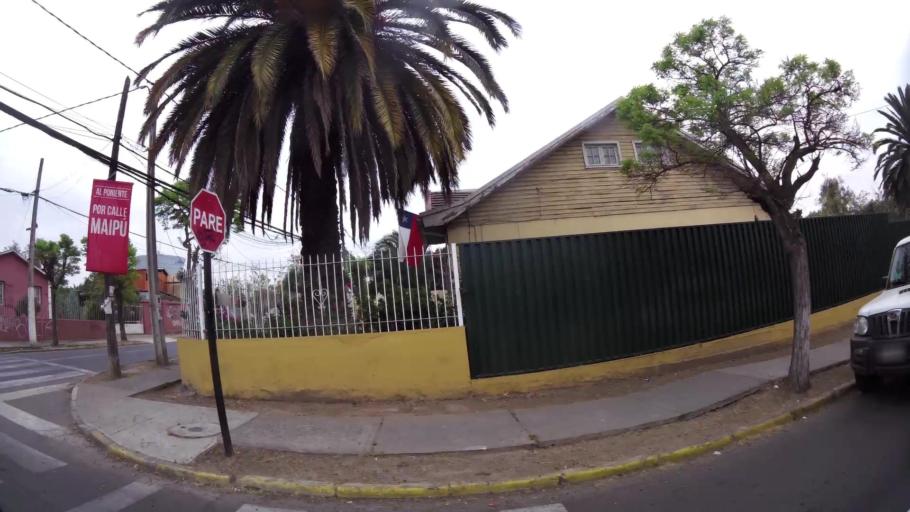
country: CL
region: Santiago Metropolitan
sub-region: Provincia de Santiago
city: Lo Prado
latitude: -33.5055
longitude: -70.7619
